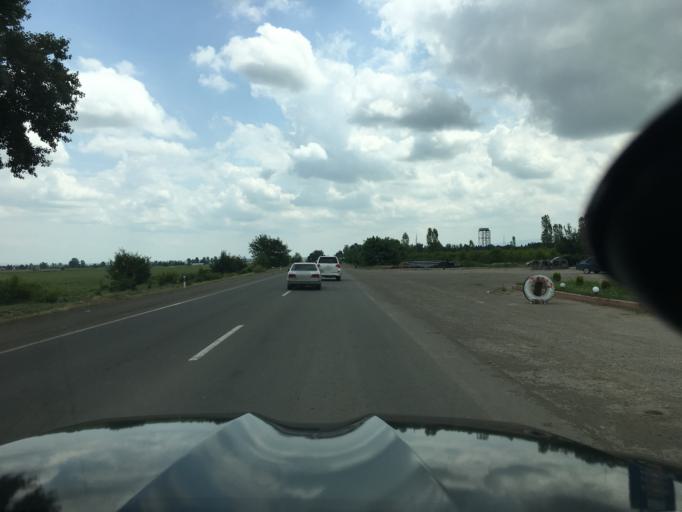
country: AZ
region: Tovuz
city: Tovuz
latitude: 40.9624
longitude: 45.7153
